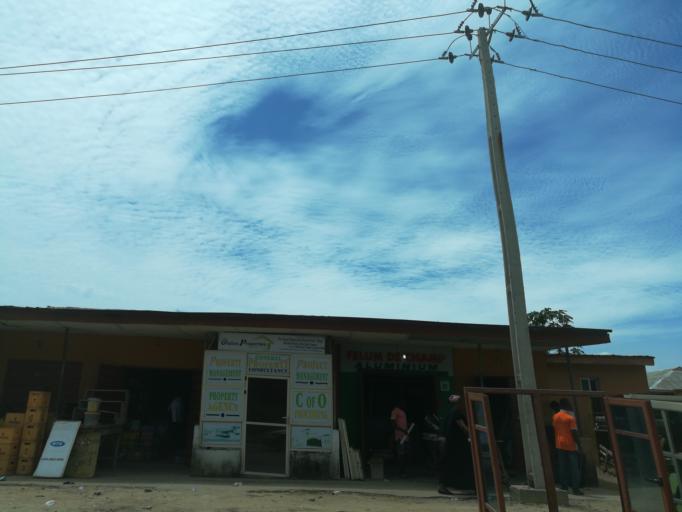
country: NG
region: Lagos
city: Ebute Ikorodu
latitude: 6.5804
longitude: 3.4892
